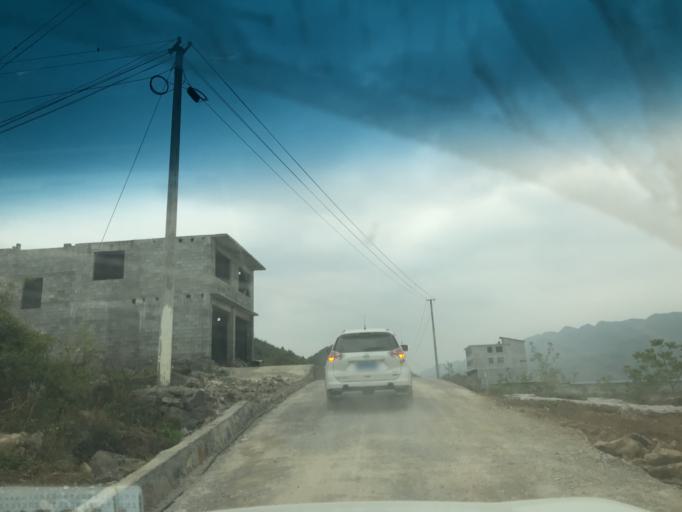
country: CN
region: Guizhou Sheng
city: Changfeng
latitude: 28.4234
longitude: 108.1318
